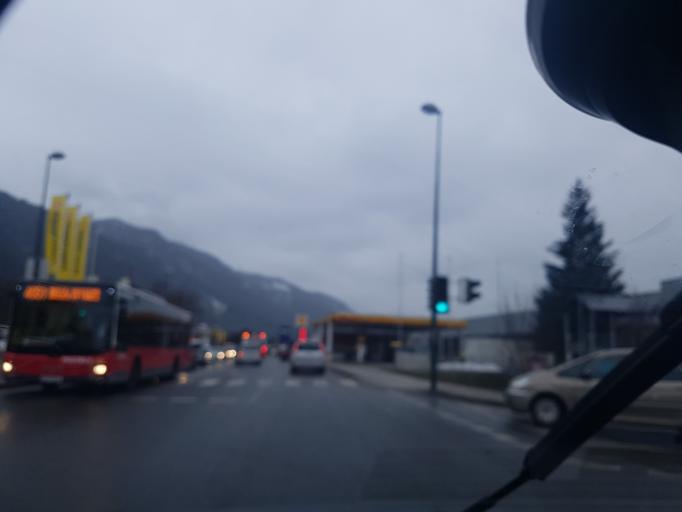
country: AT
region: Tyrol
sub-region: Politischer Bezirk Kufstein
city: Worgl
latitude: 47.4836
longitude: 12.0599
